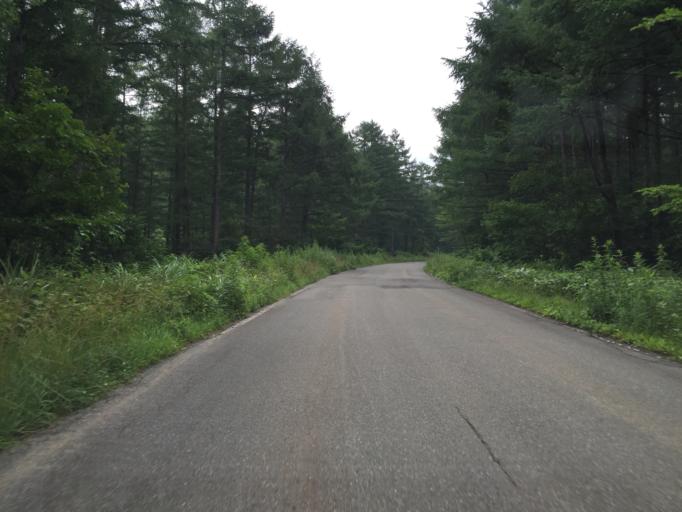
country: JP
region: Fukushima
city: Inawashiro
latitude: 37.6530
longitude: 140.1774
